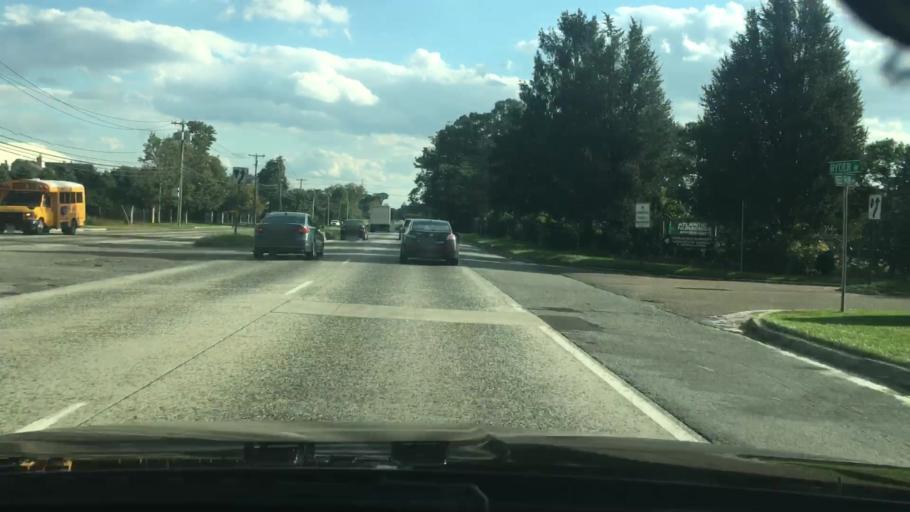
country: US
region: New York
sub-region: Suffolk County
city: Dix Hills
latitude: 40.7858
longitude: -73.3395
